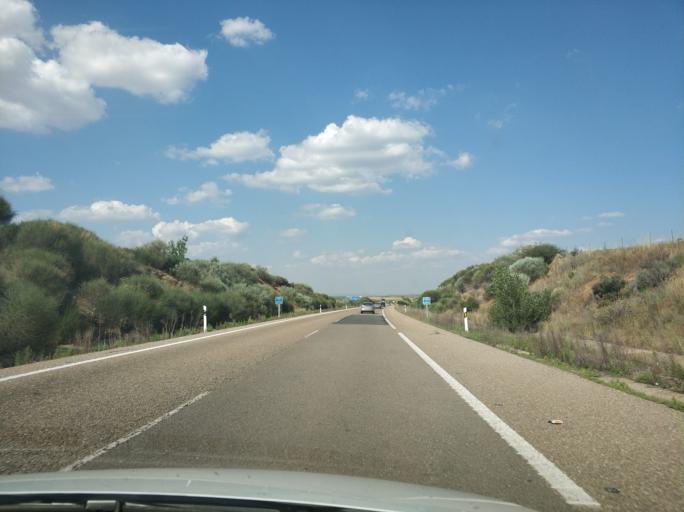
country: ES
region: Castille and Leon
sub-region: Provincia de Zamora
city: San Cristobal de Entrevinas
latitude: 42.0604
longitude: -5.6717
